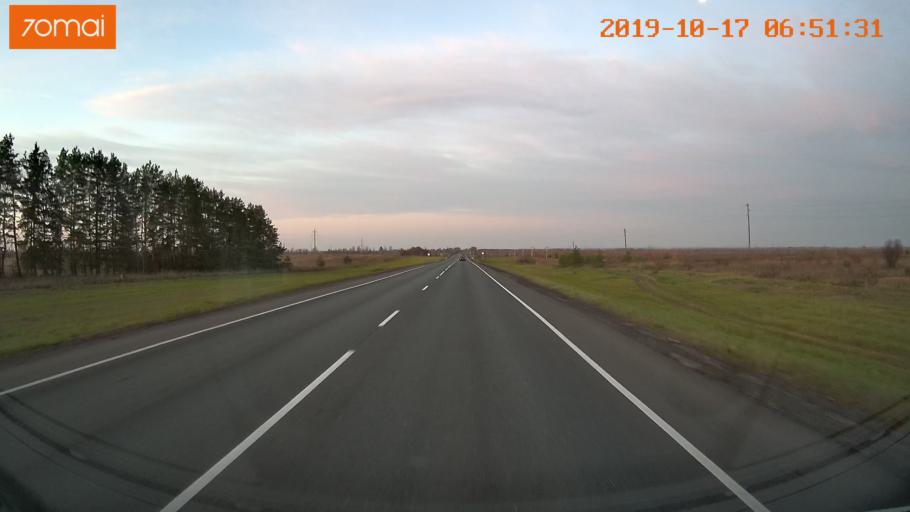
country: RU
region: Vladimir
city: Kideksha
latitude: 56.4948
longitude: 40.5255
